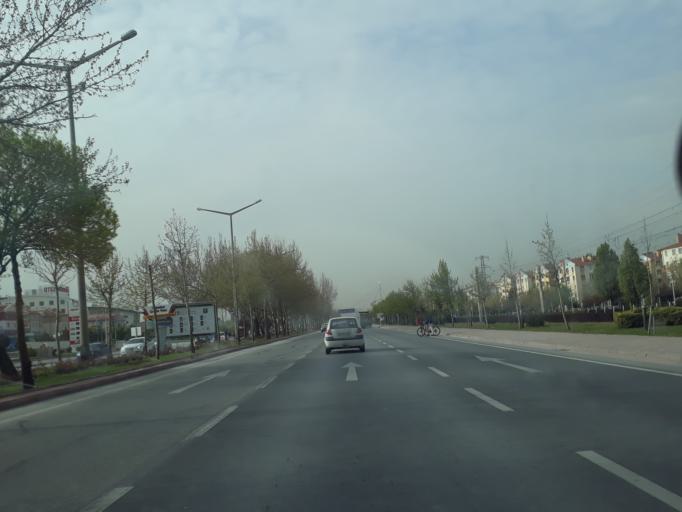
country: TR
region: Konya
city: Selcuklu
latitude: 37.9698
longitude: 32.5155
